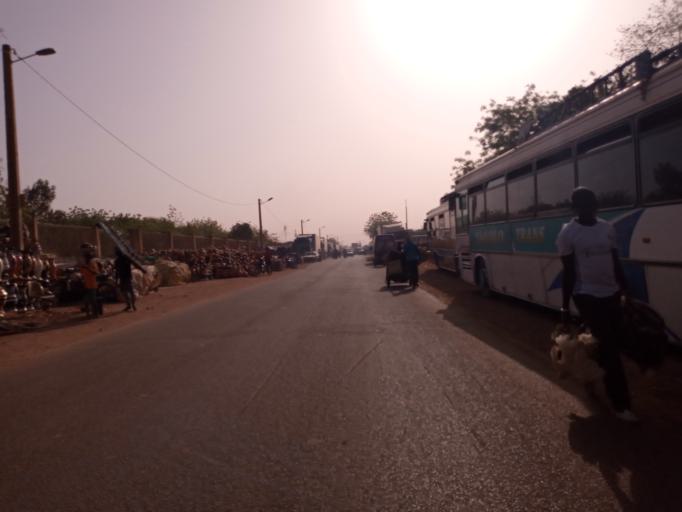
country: ML
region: Bamako
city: Bamako
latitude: 12.6585
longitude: -7.9911
